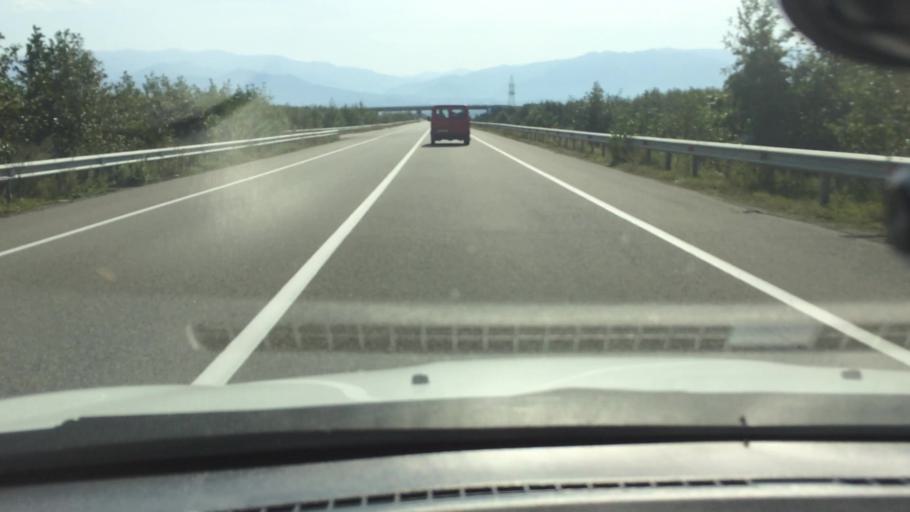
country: GE
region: Ajaria
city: Ochkhamuri
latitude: 41.8955
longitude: 41.8010
